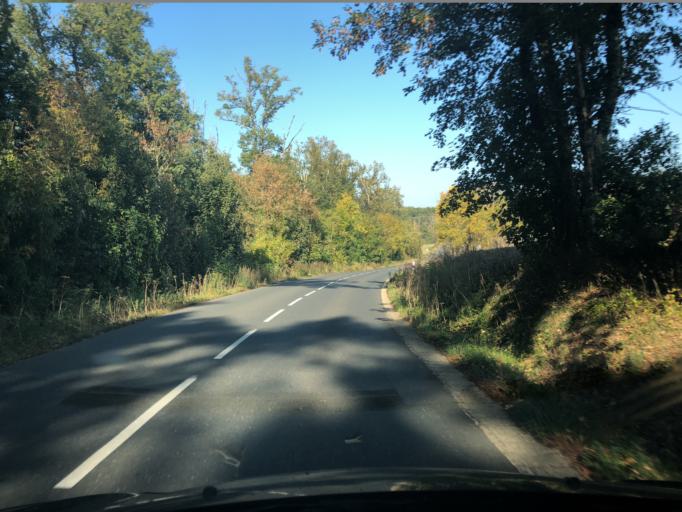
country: FR
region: Centre
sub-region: Departement d'Indre-et-Loire
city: Mettray
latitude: 47.4748
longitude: 0.6630
